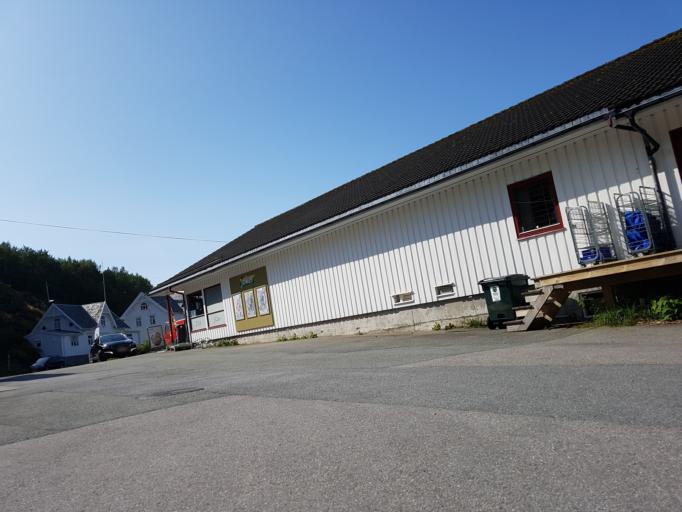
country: NO
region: Sor-Trondelag
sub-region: Agdenes
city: Lensvik
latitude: 63.6327
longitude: 9.8282
